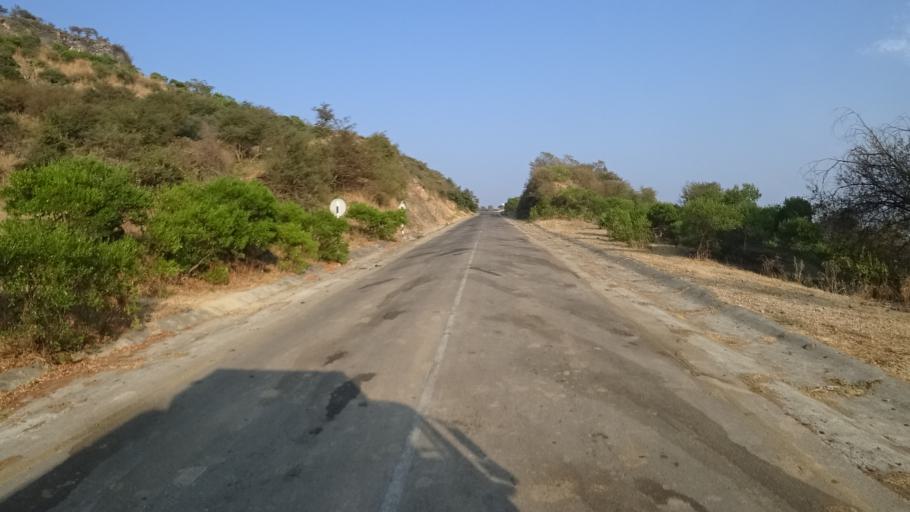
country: YE
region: Al Mahrah
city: Hawf
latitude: 16.7636
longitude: 53.3366
